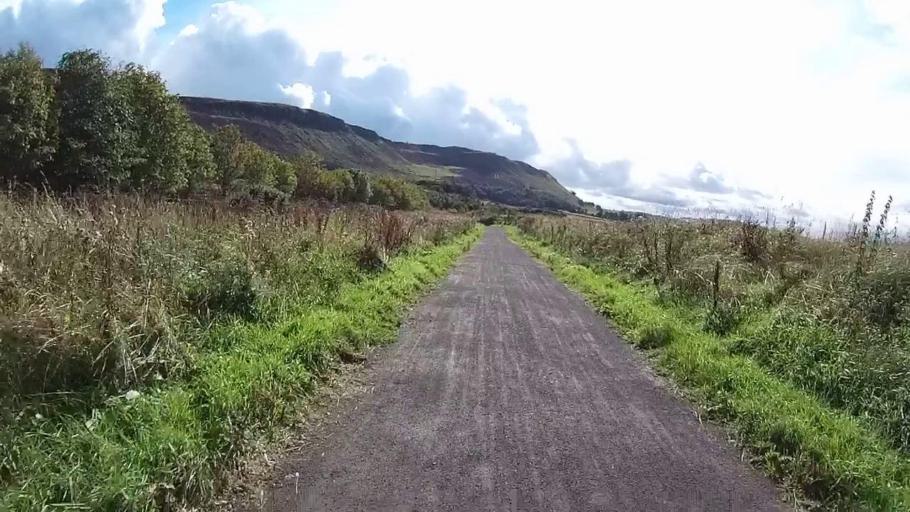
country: GB
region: Scotland
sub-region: Fife
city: Ballingry
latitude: 56.1762
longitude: -3.3568
